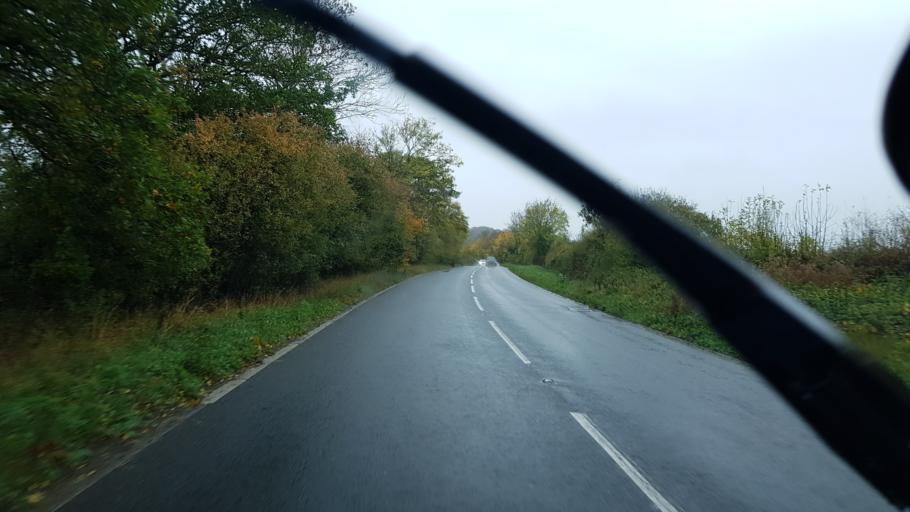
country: GB
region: England
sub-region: Gloucestershire
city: Stow on the Wold
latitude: 51.9107
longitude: -1.7217
